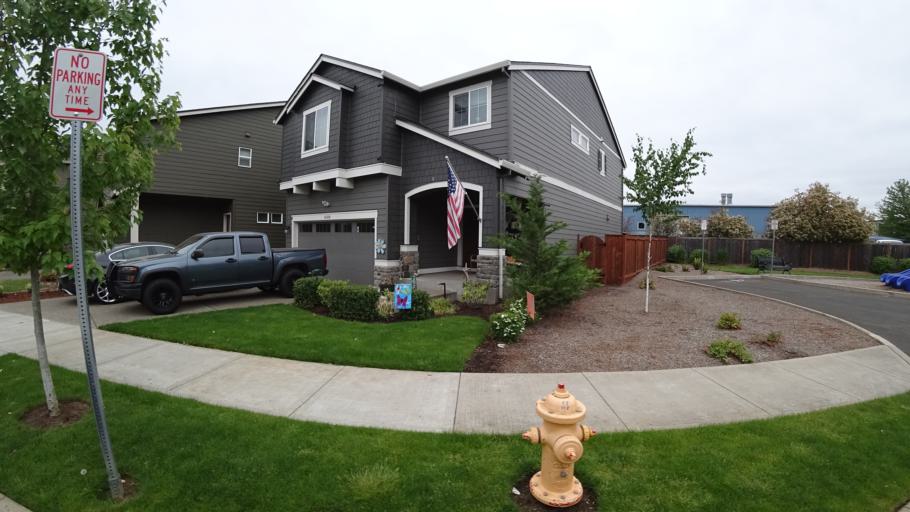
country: US
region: Oregon
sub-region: Washington County
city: Aloha
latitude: 45.4948
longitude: -122.9170
